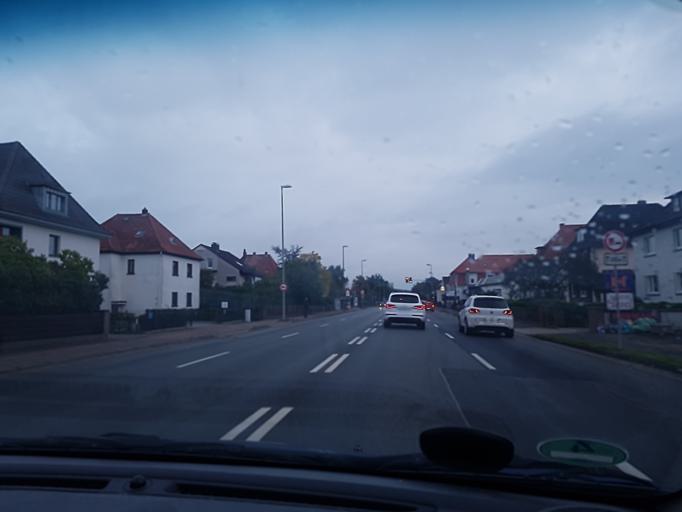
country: DE
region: Lower Saxony
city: Hemmingen
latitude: 52.3261
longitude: 9.7227
